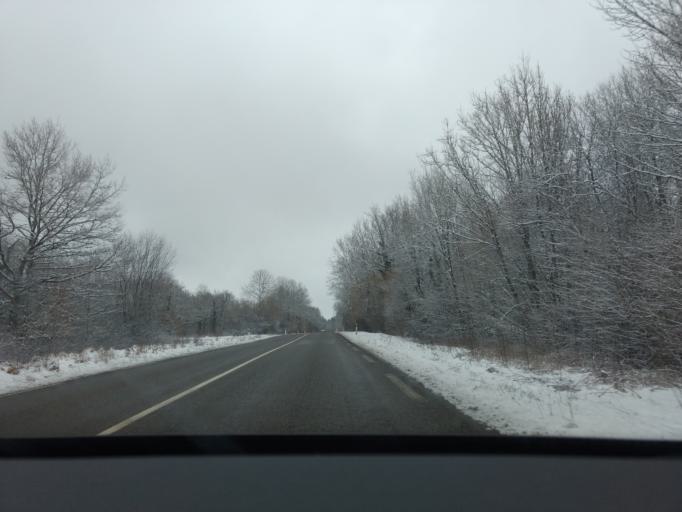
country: FR
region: Franche-Comte
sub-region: Departement du Jura
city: Champagnole
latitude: 46.7830
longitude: 5.8622
